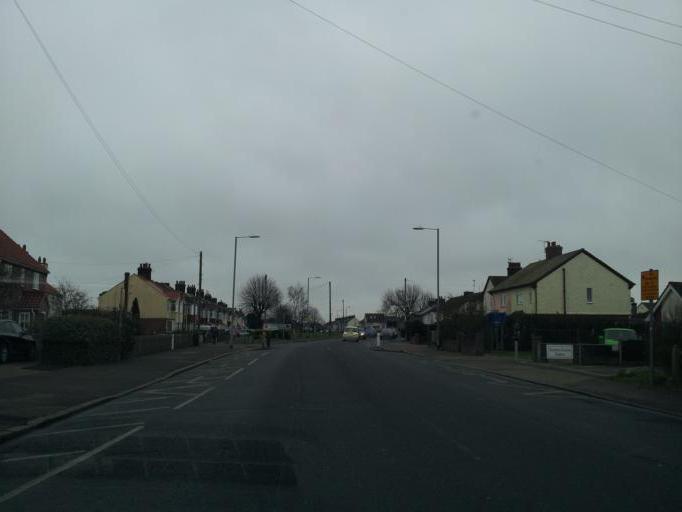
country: GB
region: England
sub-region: Essex
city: Dovercourt
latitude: 51.9309
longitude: 1.2456
